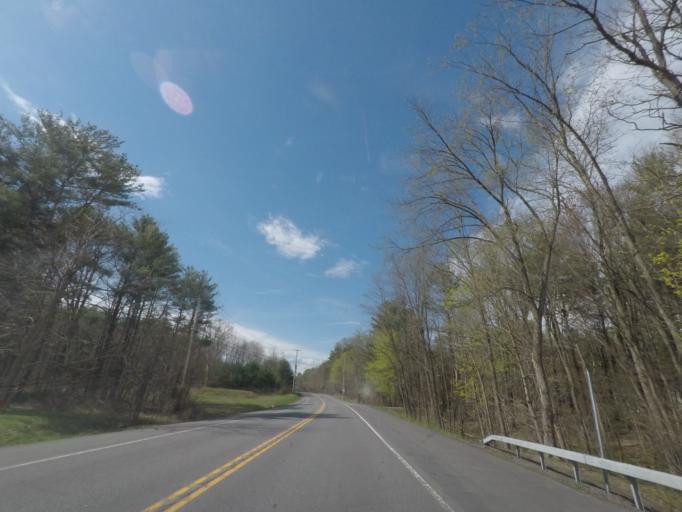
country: US
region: New York
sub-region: Greene County
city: Cairo
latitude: 42.3091
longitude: -74.0051
